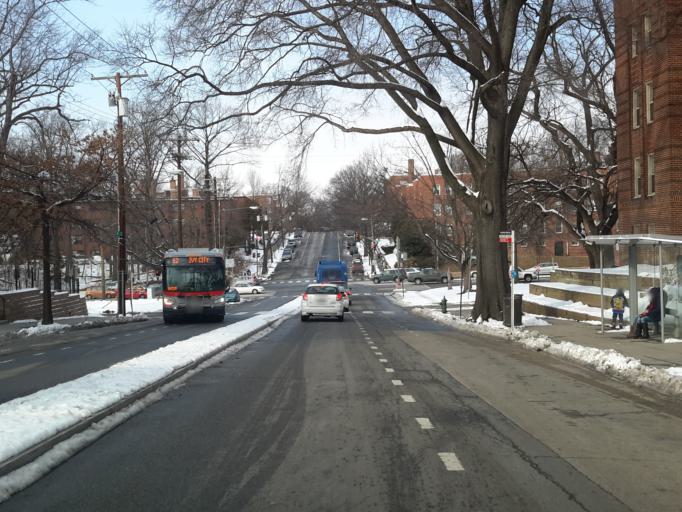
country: US
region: Maryland
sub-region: Montgomery County
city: Silver Spring
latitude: 38.9611
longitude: -77.0334
